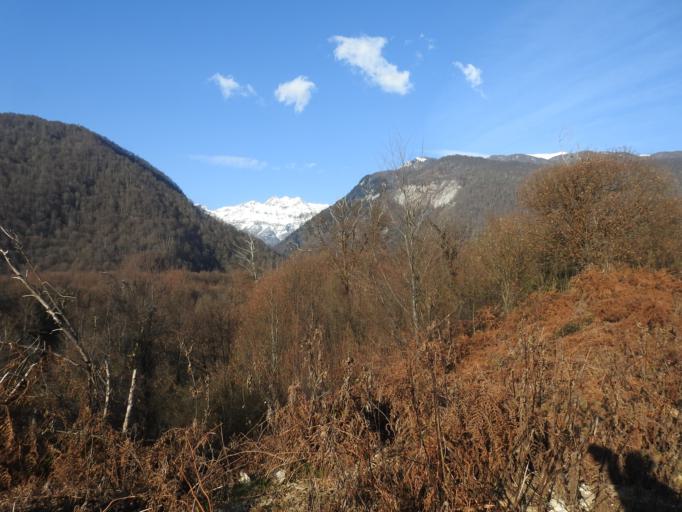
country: GE
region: Abkhazia
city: Gudauta
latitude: 43.2263
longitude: 40.6568
